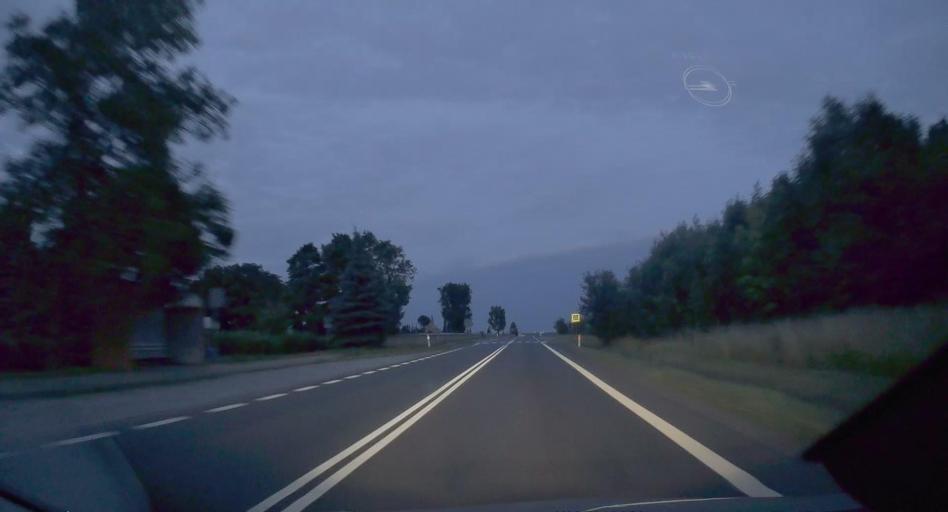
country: PL
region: Silesian Voivodeship
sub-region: Powiat klobucki
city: Klobuck
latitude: 50.8963
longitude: 18.9501
